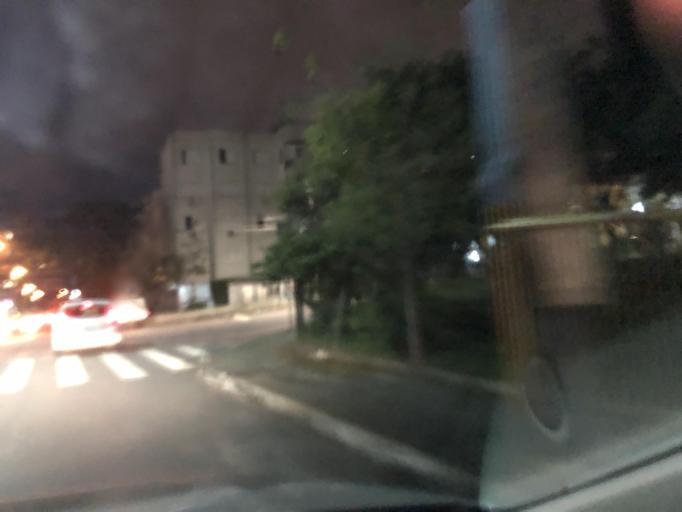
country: BR
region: Santa Catarina
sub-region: Florianopolis
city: Carvoeira
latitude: -27.6021
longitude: -48.5260
